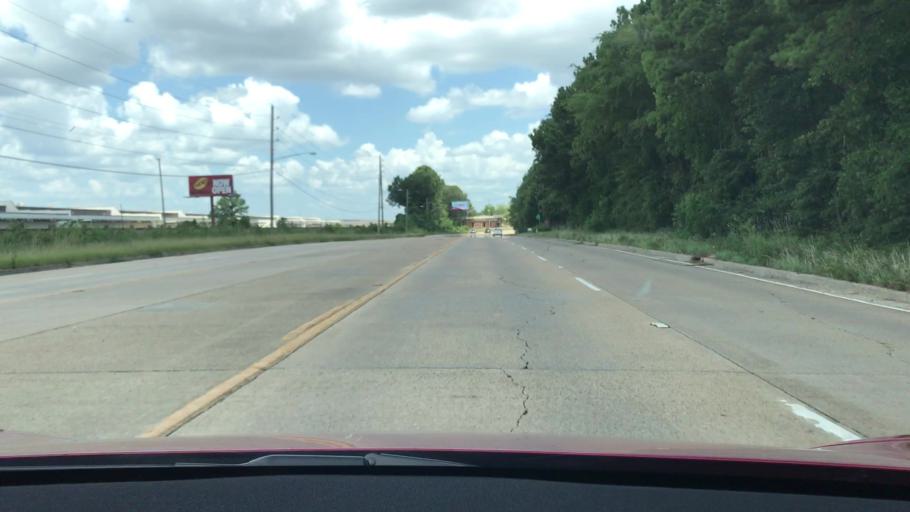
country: US
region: Louisiana
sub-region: Bossier Parish
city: Bossier City
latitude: 32.4033
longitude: -93.7368
